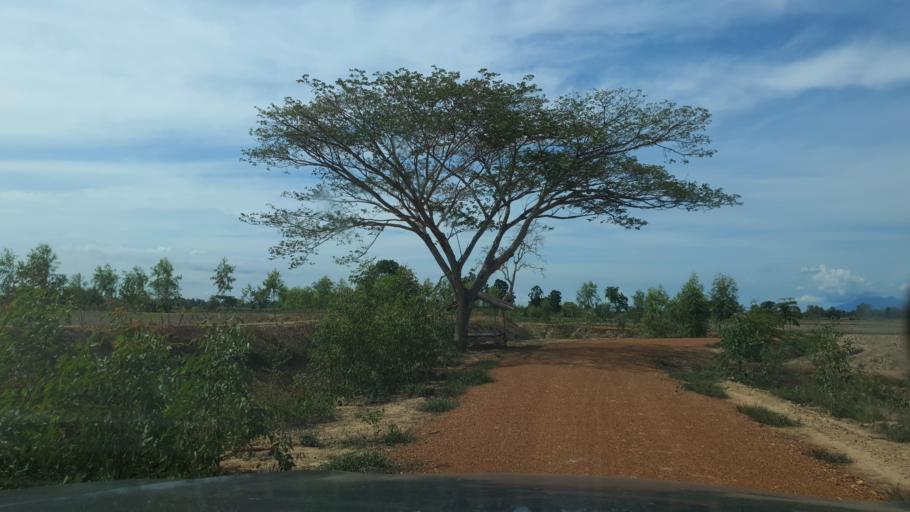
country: TH
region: Sukhothai
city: Thung Saliam
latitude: 17.2522
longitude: 99.6624
